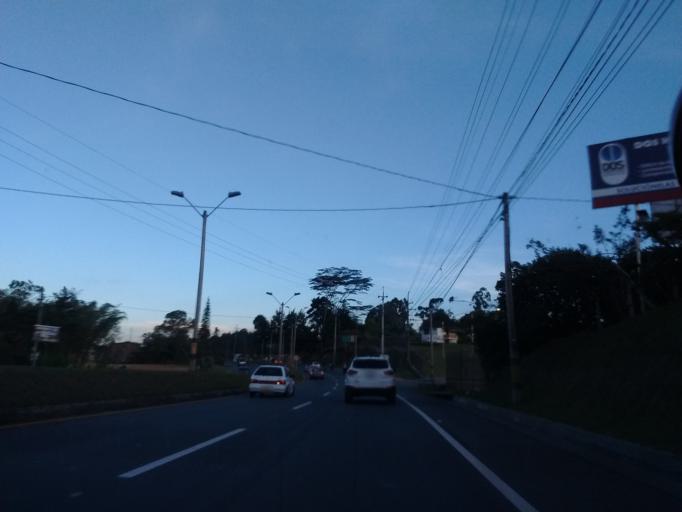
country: CO
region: Antioquia
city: Rionegro
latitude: 6.1892
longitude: -75.3808
